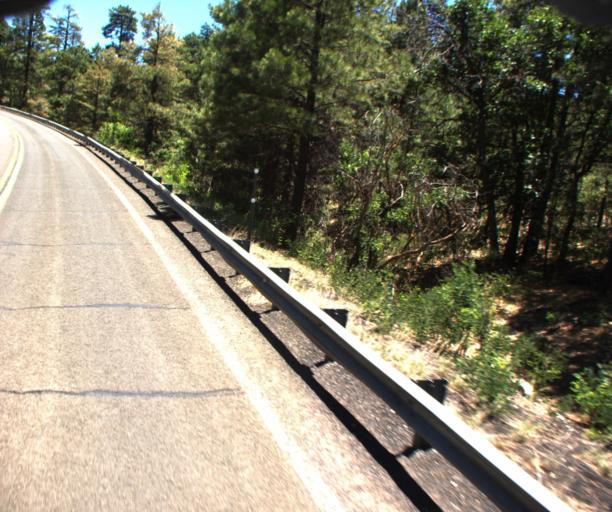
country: US
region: Arizona
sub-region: Gila County
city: Pine
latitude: 34.6057
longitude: -111.2263
